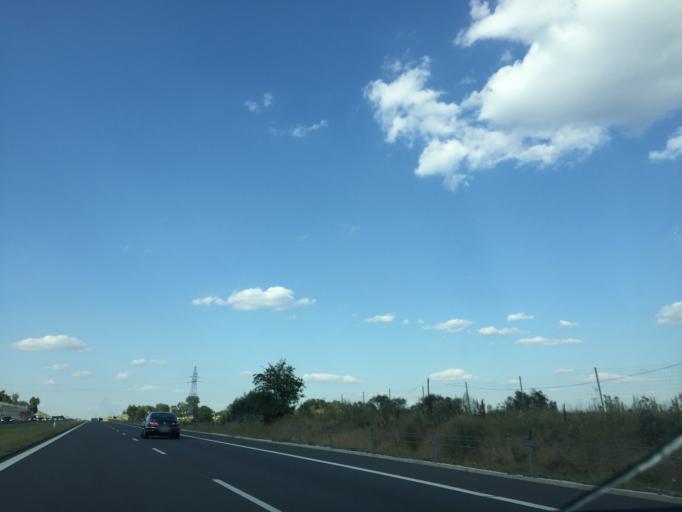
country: PL
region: Swietokrzyskie
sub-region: Powiat kielecki
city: Checiny
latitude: 50.7833
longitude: 20.4695
